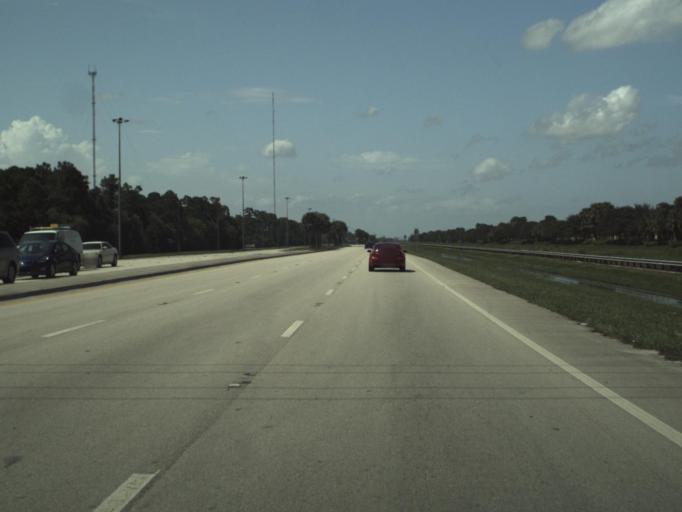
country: US
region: Florida
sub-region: Palm Beach County
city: Wellington
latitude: 26.5707
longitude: -80.2057
